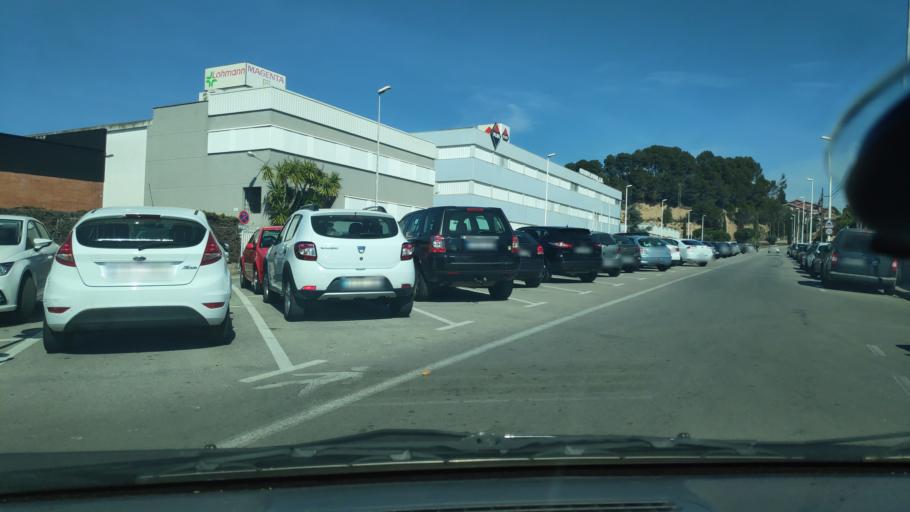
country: ES
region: Catalonia
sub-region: Provincia de Barcelona
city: Rubi
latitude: 41.5031
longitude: 2.0438
